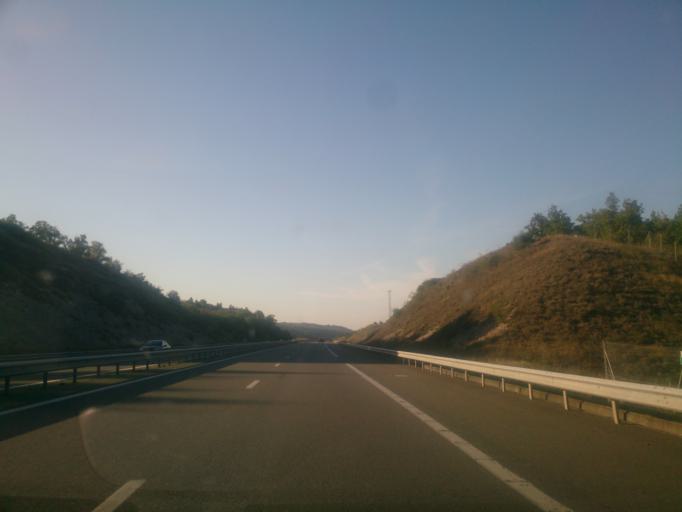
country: FR
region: Midi-Pyrenees
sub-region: Departement du Lot
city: Le Vigan
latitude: 44.8036
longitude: 1.5065
